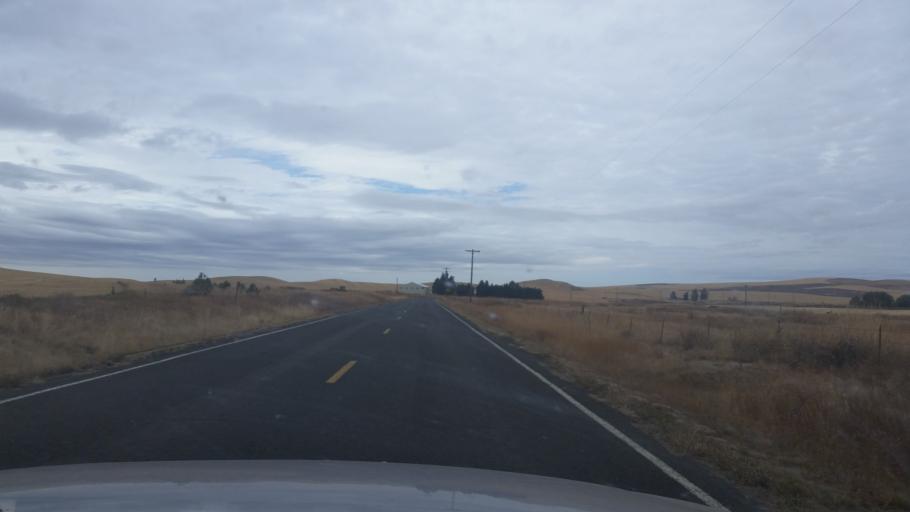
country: US
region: Washington
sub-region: Spokane County
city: Medical Lake
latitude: 47.5176
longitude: -117.8912
